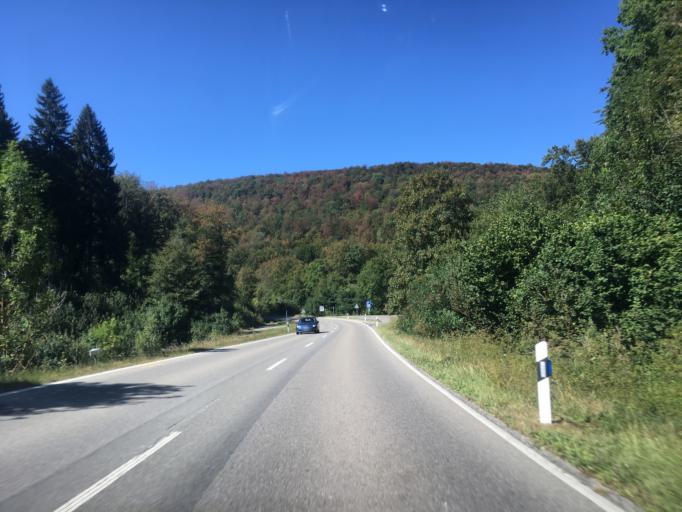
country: DE
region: Baden-Wuerttemberg
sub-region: Tuebingen Region
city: Pfullingen
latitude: 48.3989
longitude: 9.2641
